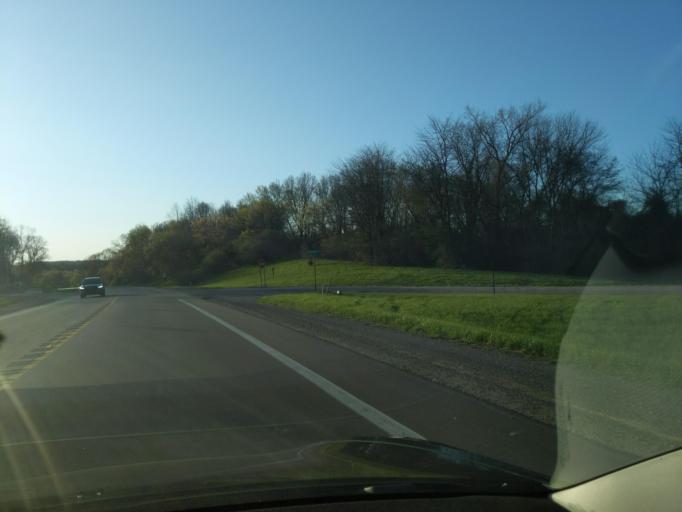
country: US
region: Michigan
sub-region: Washtenaw County
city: Chelsea
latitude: 42.3462
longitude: -84.0413
